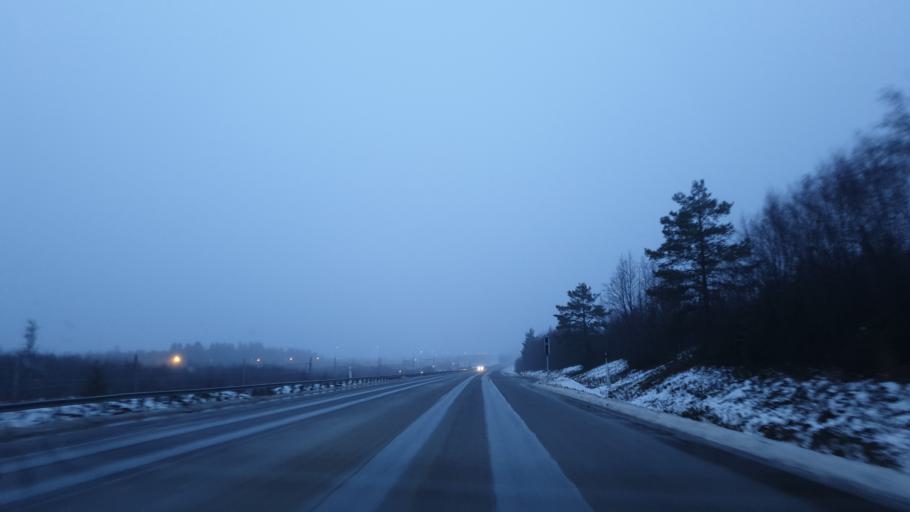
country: SE
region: Vaesterbotten
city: Obbola
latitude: 63.7792
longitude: 20.3248
